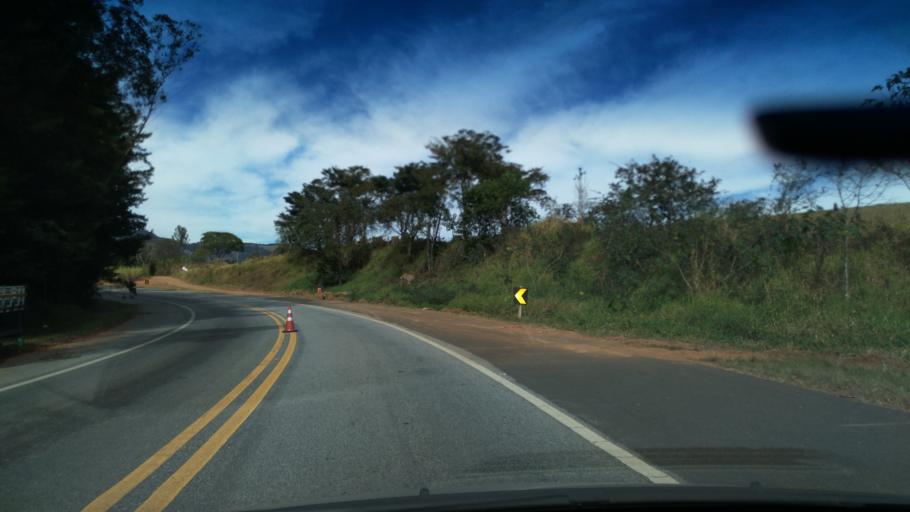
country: BR
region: Minas Gerais
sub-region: Borda Da Mata
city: Borda da Mata
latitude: -22.1493
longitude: -46.1292
